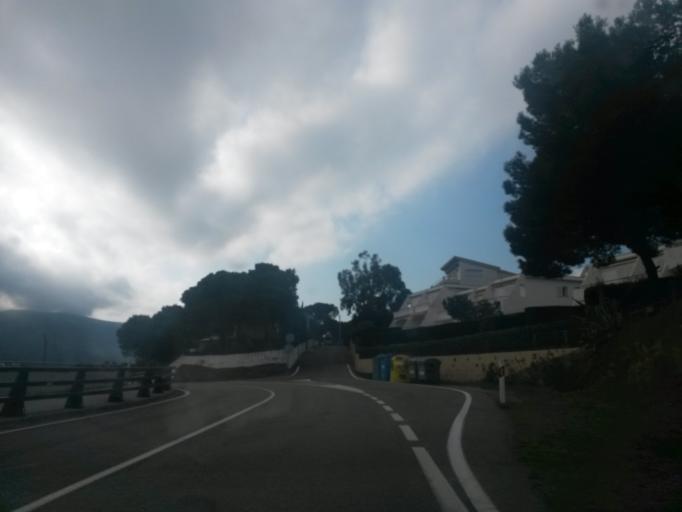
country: ES
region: Catalonia
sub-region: Provincia de Girona
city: Llanca
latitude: 42.3831
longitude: 3.1575
